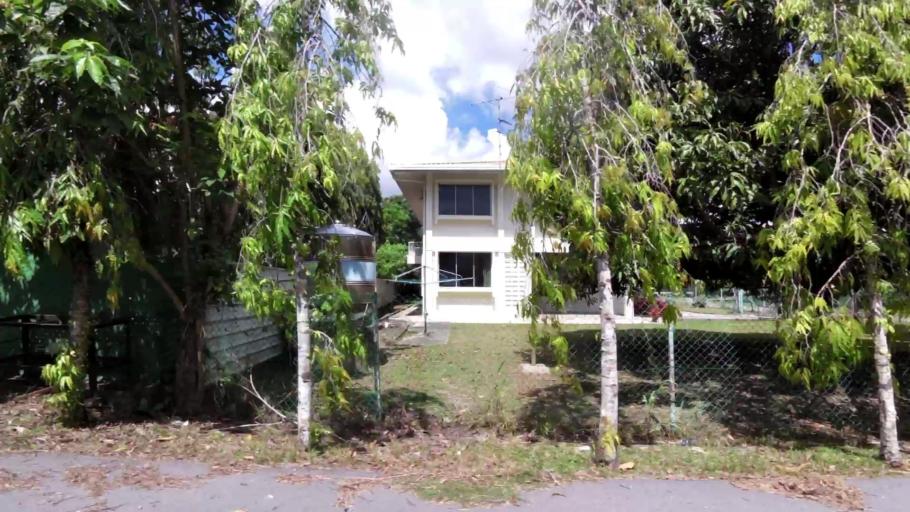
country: BN
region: Brunei and Muara
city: Bandar Seri Begawan
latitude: 4.9731
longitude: 114.9424
